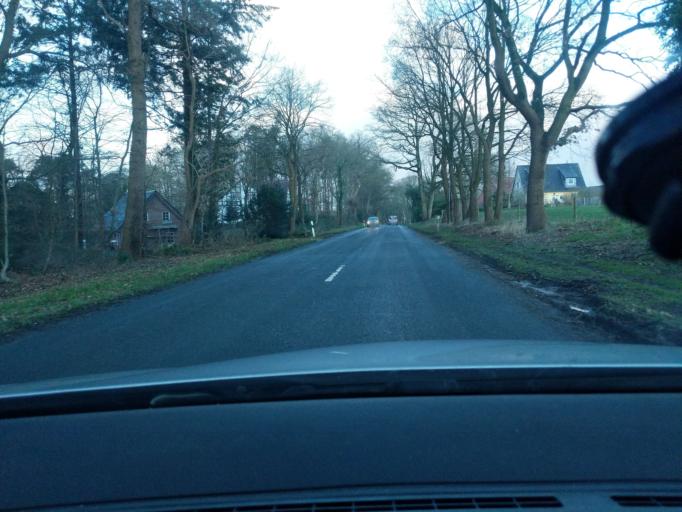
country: DE
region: Lower Saxony
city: Drangstedt
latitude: 53.6408
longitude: 8.7825
